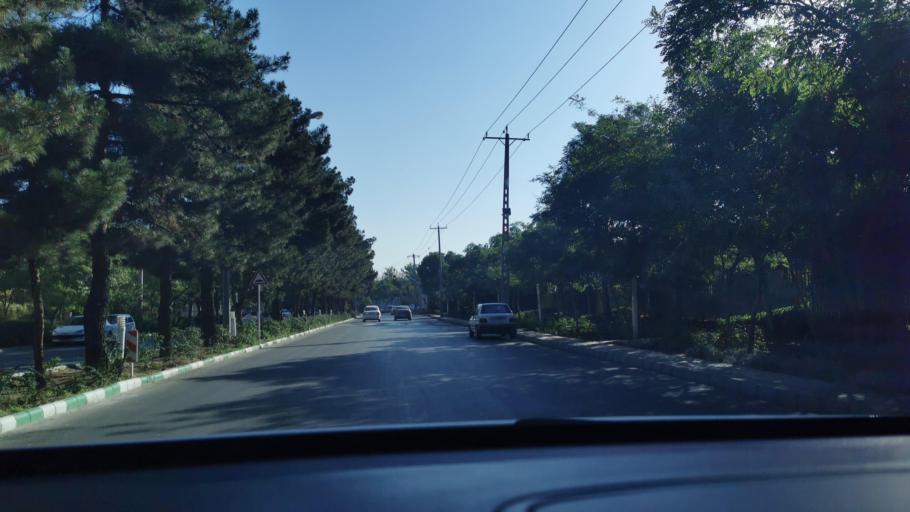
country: IR
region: Razavi Khorasan
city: Mashhad
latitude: 36.3146
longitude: 59.5250
